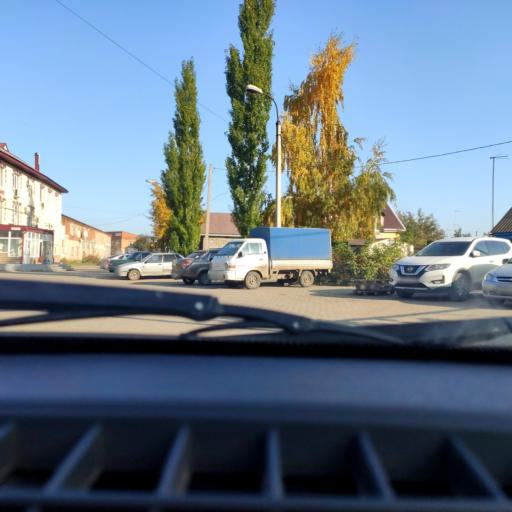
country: RU
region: Bashkortostan
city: Ufa
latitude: 54.7823
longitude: 56.0599
